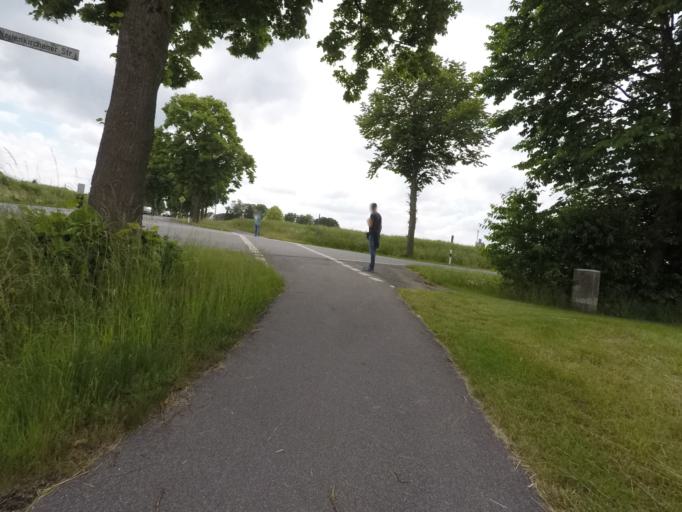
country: DE
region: North Rhine-Westphalia
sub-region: Regierungsbezirk Detmold
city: Werther
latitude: 52.1015
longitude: 8.4537
